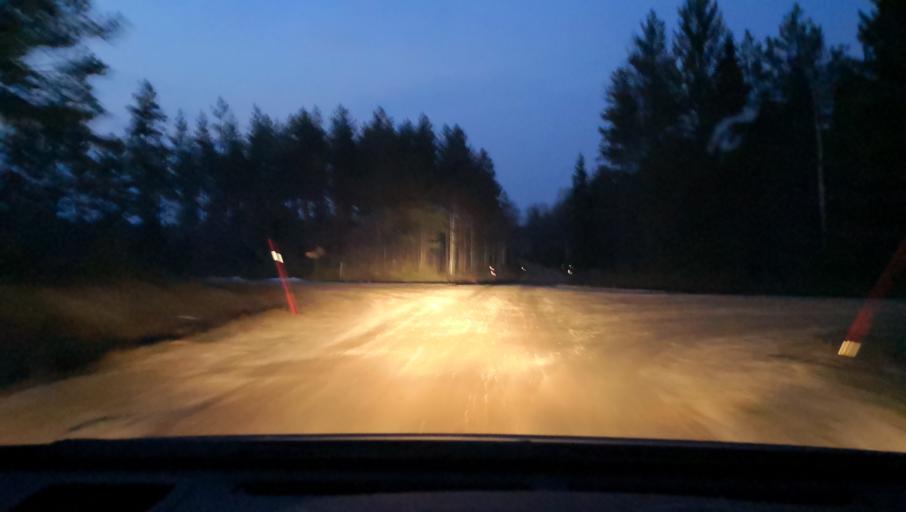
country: SE
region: OErebro
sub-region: Lindesbergs Kommun
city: Frovi
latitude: 59.6086
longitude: 15.4770
